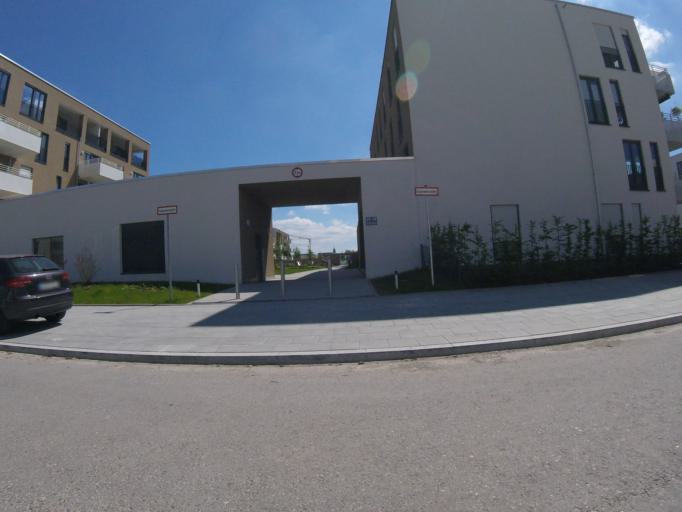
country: DE
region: Bavaria
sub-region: Upper Bavaria
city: Unterhaching
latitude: 48.1017
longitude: 11.6201
